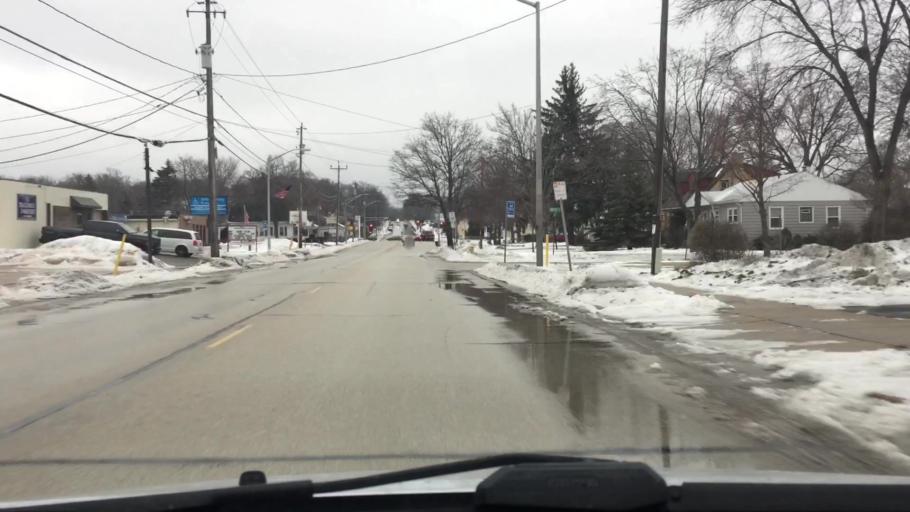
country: US
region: Wisconsin
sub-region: Waukesha County
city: Waukesha
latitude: 43.0242
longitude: -88.2559
